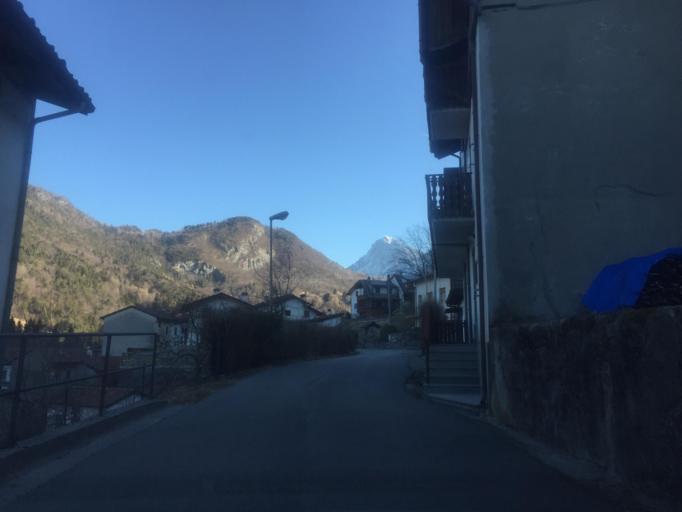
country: IT
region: Friuli Venezia Giulia
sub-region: Provincia di Udine
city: Zuglio
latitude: 46.4287
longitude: 13.0572
